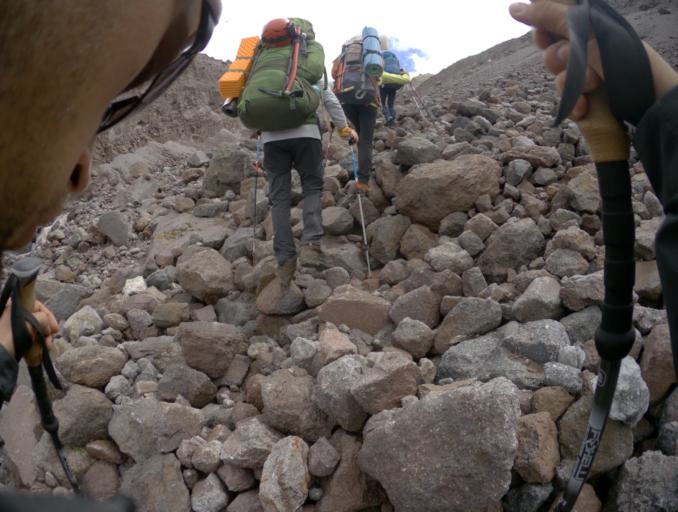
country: RU
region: Kabardino-Balkariya
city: Terskol
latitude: 43.3836
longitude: 42.3706
